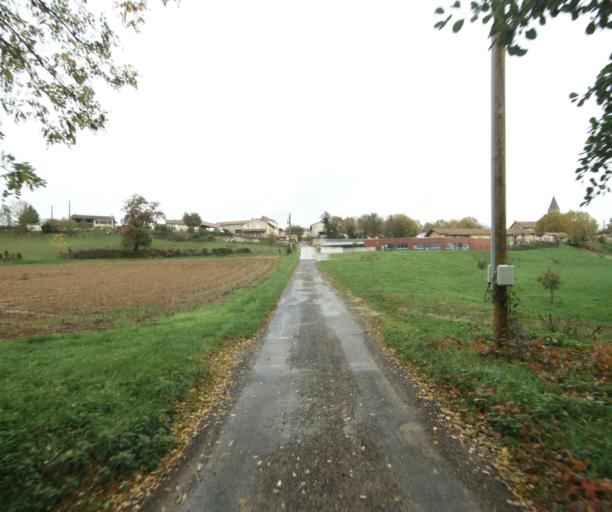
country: FR
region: Rhone-Alpes
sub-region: Departement de l'Ain
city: Pont-de-Vaux
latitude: 46.4741
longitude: 4.8731
